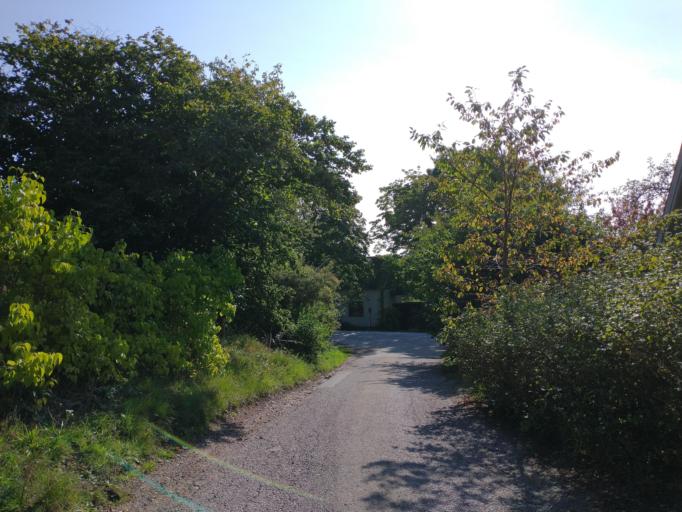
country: SE
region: Kalmar
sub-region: Kalmar Kommun
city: Lindsdal
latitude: 56.7837
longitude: 16.2897
